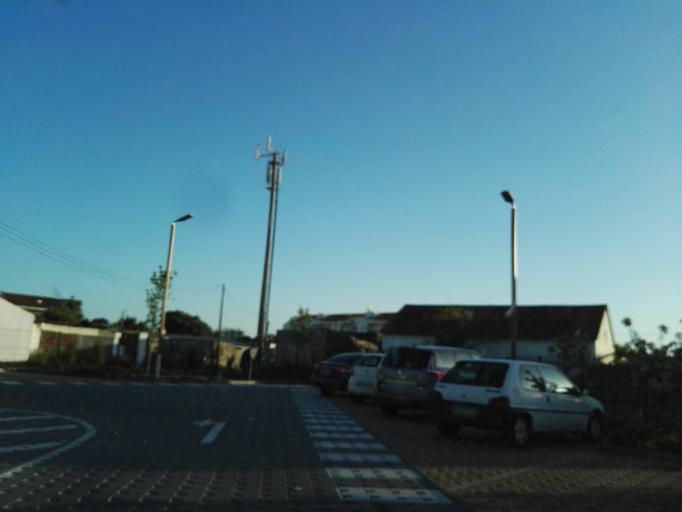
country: PT
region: Santarem
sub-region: Benavente
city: Samora Correia
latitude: 38.9221
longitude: -8.8853
